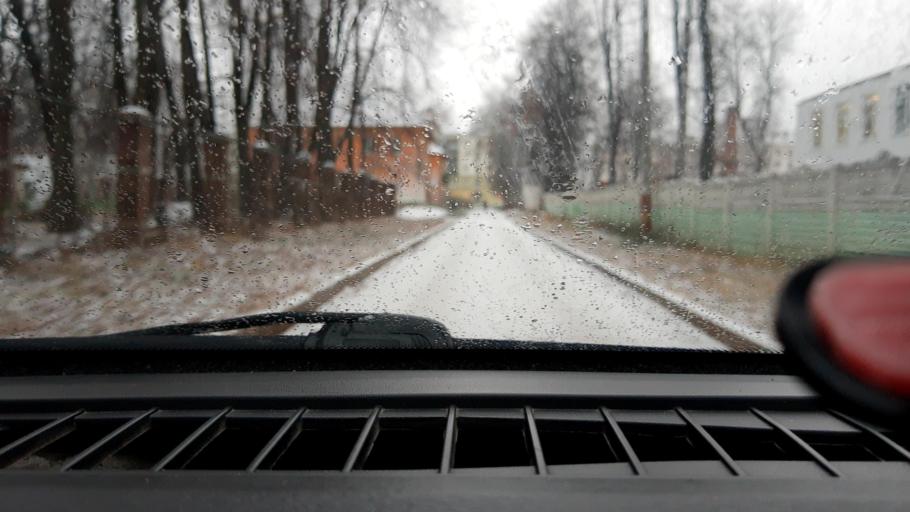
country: RU
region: Nizjnij Novgorod
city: Kstovo
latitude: 56.1478
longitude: 44.2019
